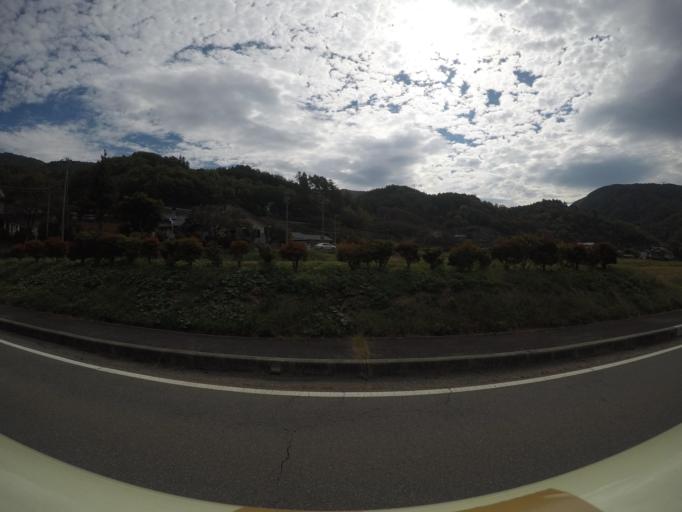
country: JP
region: Nagano
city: Ina
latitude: 35.8606
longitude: 138.0869
